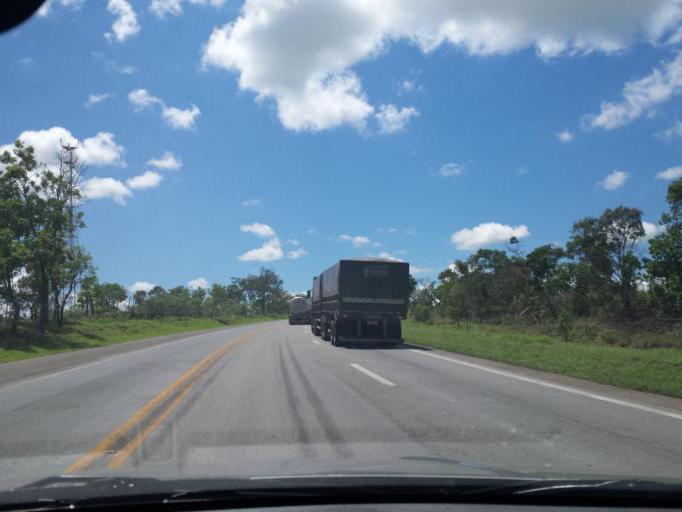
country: BR
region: Goias
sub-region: Cristalina
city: Cristalina
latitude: -16.5455
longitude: -47.7882
